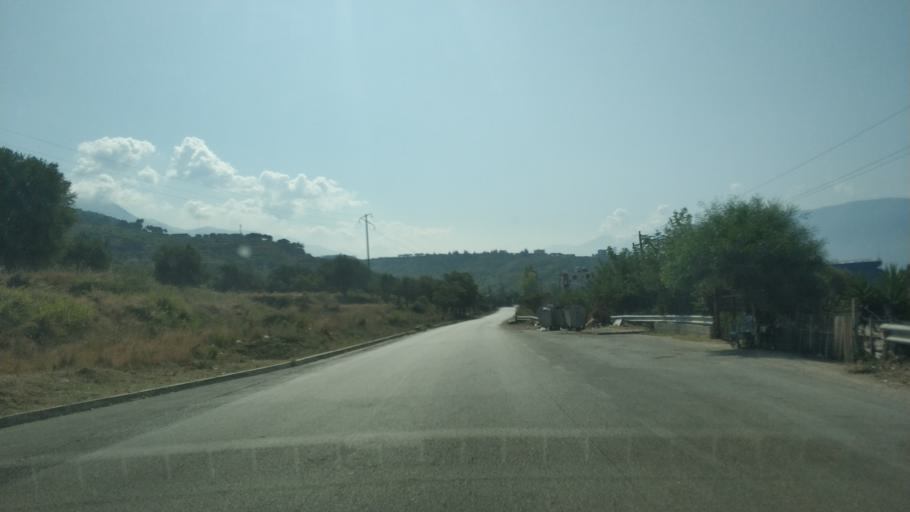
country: AL
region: Vlore
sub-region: Rrethi i Vlores
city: Orikum
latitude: 40.3764
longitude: 19.4816
